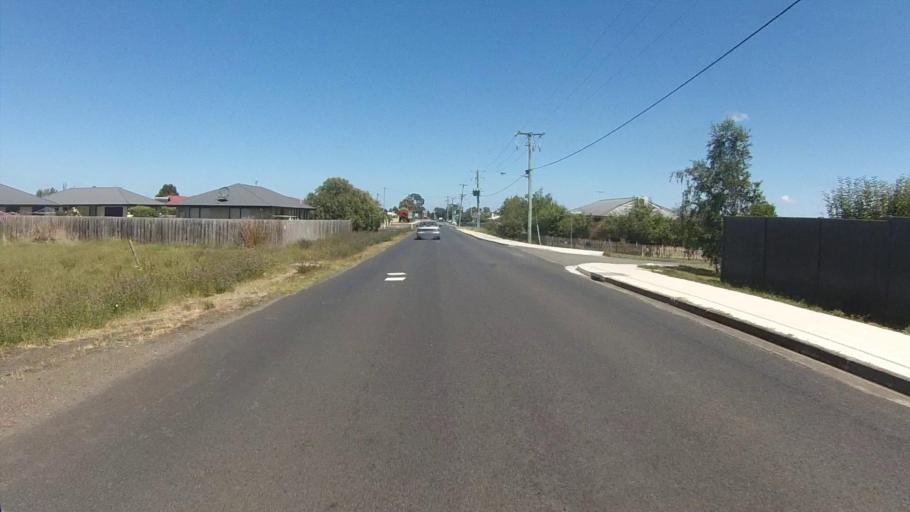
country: AU
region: Tasmania
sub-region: Sorell
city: Sorell
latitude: -42.7789
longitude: 147.5659
